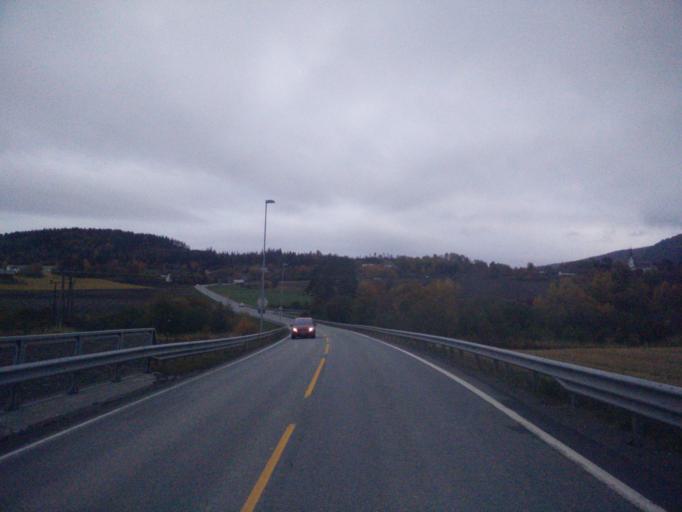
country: NO
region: Nord-Trondelag
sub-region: Stjordal
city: Stjordal
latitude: 63.5046
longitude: 10.8581
